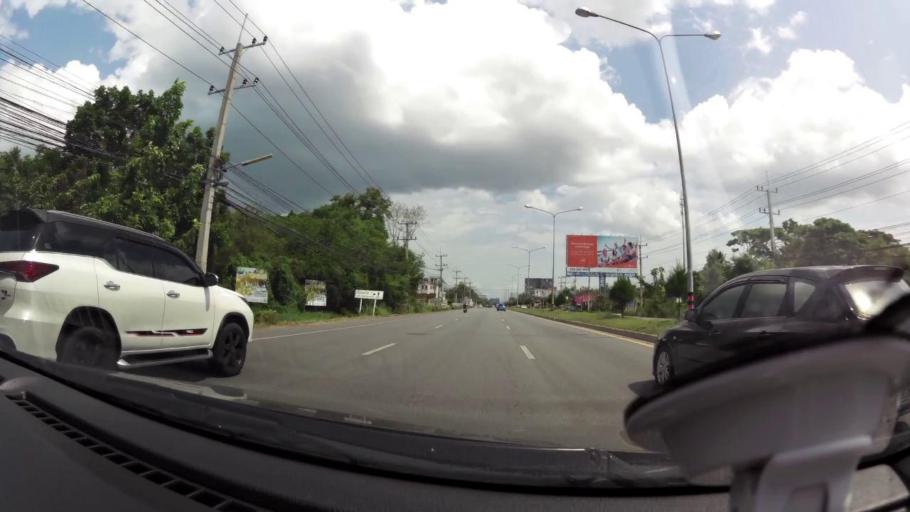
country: TH
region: Prachuap Khiri Khan
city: Hua Hin
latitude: 12.6630
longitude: 99.9523
